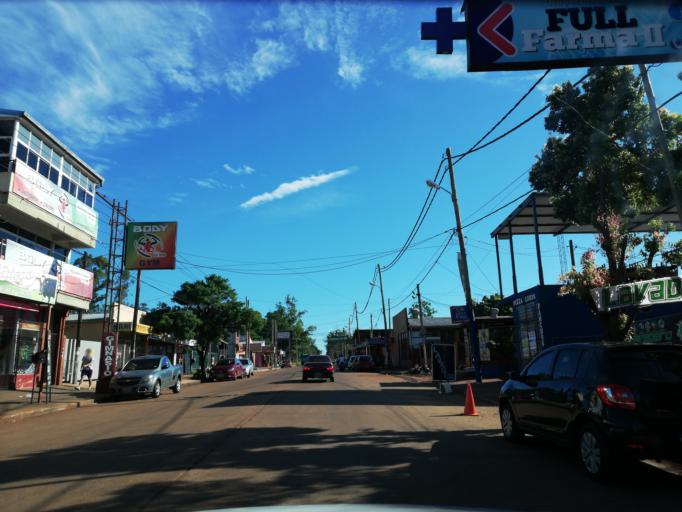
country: AR
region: Misiones
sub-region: Departamento de Capital
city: Posadas
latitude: -27.4003
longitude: -55.9518
